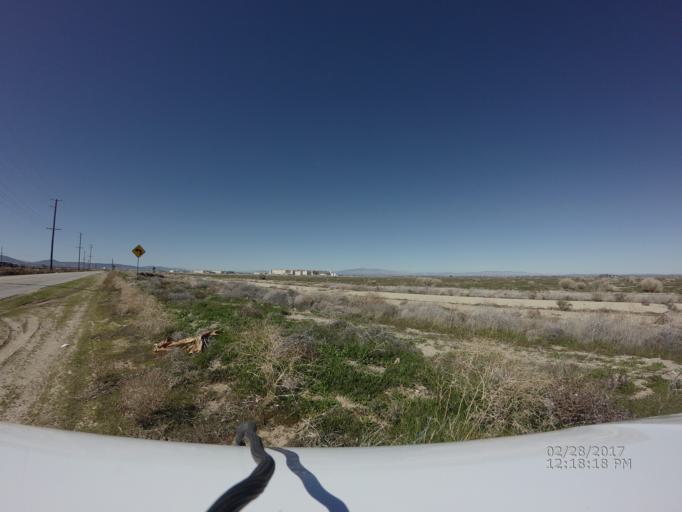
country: US
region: California
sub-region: Los Angeles County
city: Palmdale
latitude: 34.6315
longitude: -118.0551
